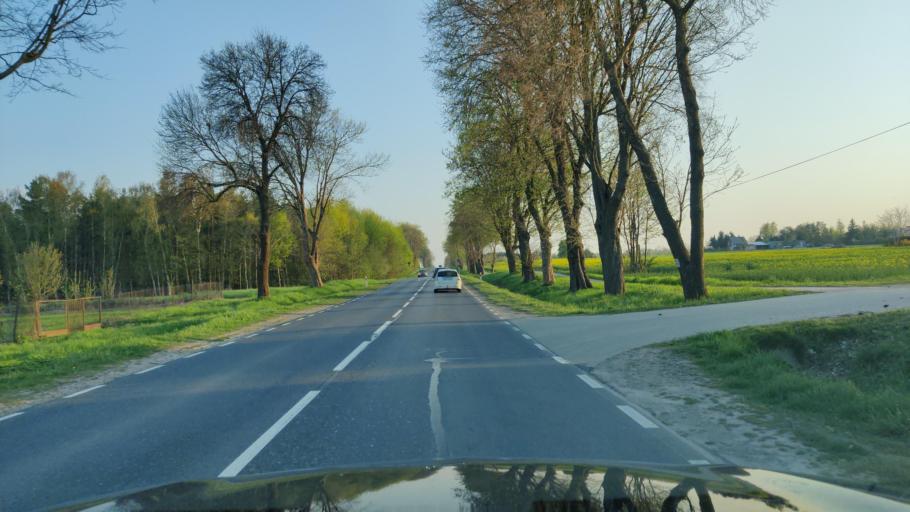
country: PL
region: Masovian Voivodeship
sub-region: Powiat legionowski
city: Serock
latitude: 52.5796
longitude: 21.0964
